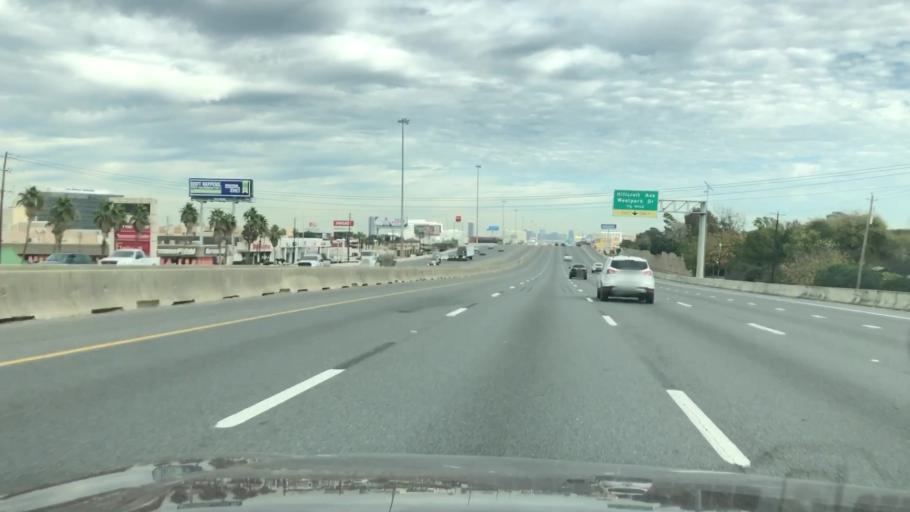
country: US
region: Texas
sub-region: Harris County
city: Bellaire
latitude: 29.7011
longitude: -95.5166
